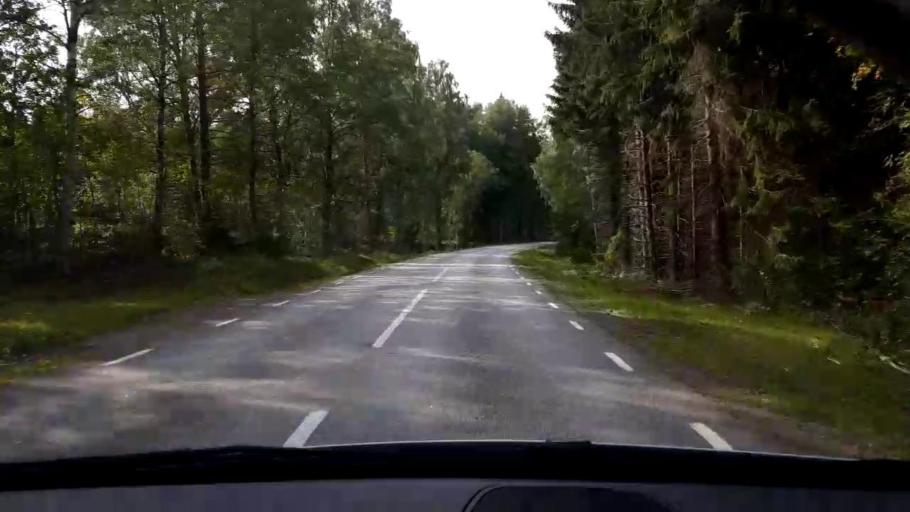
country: SE
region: Joenkoeping
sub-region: Vetlanda Kommun
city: Vetlanda
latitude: 57.3640
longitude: 15.0624
